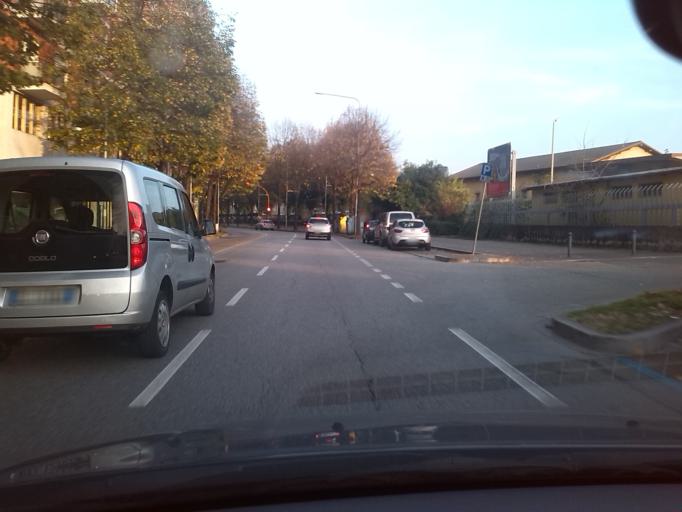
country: IT
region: Friuli Venezia Giulia
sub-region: Provincia di Udine
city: Udine
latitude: 46.0555
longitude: 13.2378
